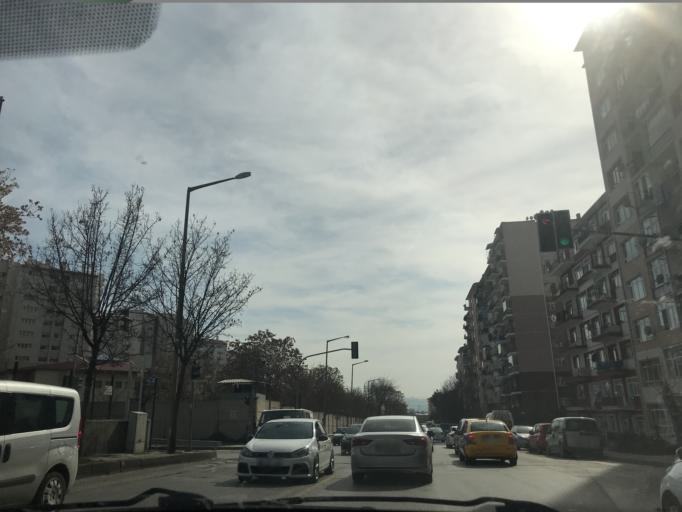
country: TR
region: Ankara
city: Batikent
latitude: 39.9615
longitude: 32.7968
